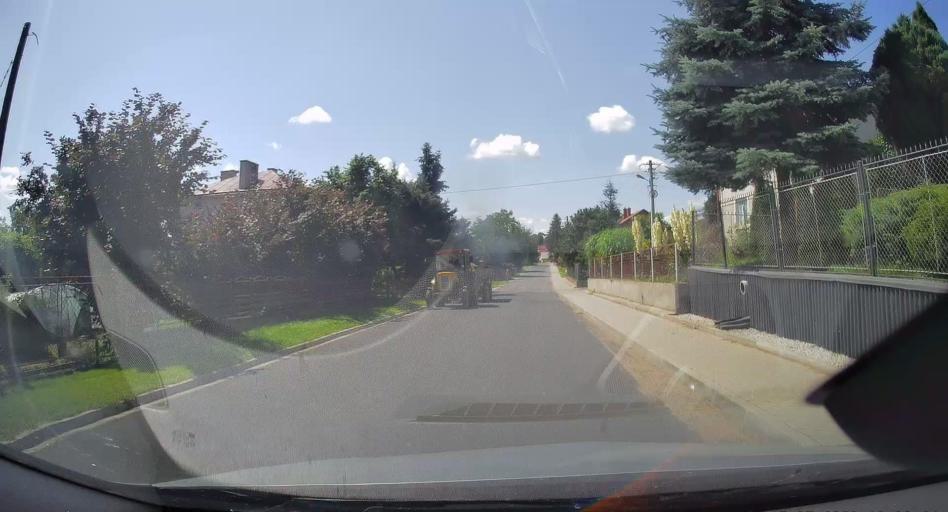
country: PL
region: Subcarpathian Voivodeship
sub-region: Powiat przemyski
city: Medyka
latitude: 49.8439
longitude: 22.8865
